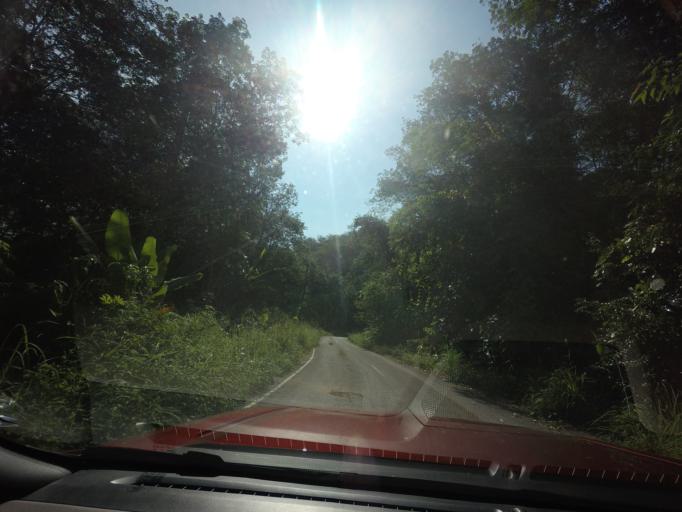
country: TH
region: Narathiwat
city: Si Sakhon
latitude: 6.0660
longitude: 101.3718
